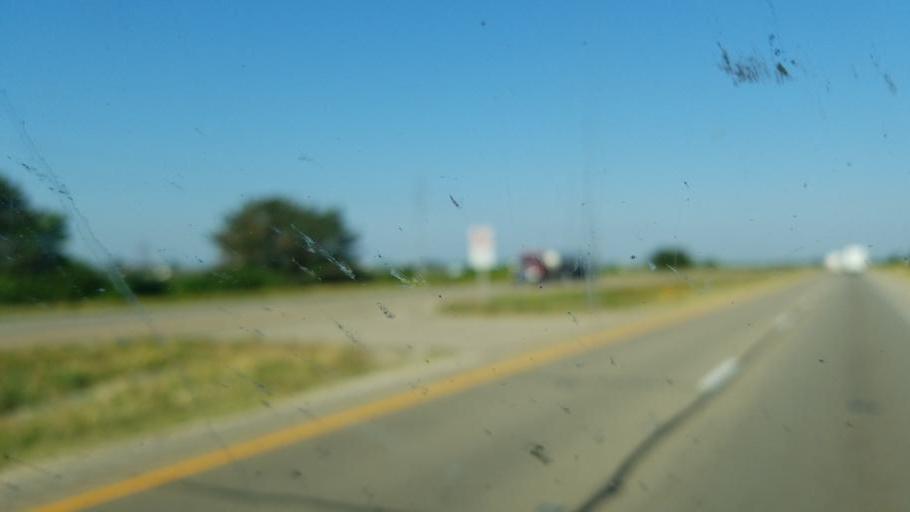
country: US
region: Illinois
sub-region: LaSalle County
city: Ottawa
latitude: 41.3682
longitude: -88.9499
